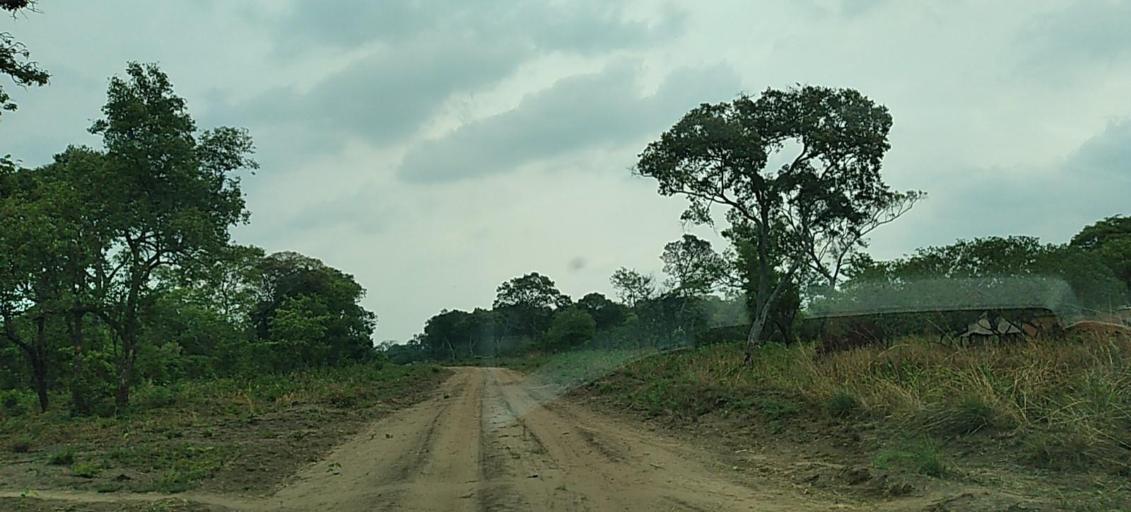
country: ZM
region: North-Western
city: Mwinilunga
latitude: -11.4185
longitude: 24.6008
